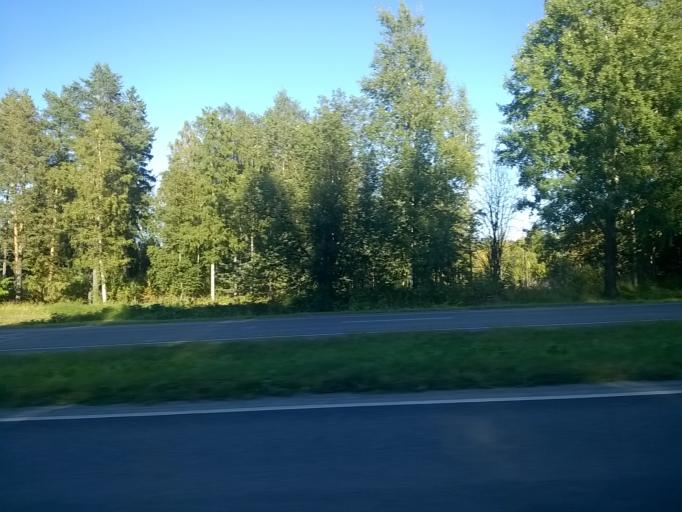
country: FI
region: Pirkanmaa
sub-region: Tampere
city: Tampere
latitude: 61.4683
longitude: 23.8411
